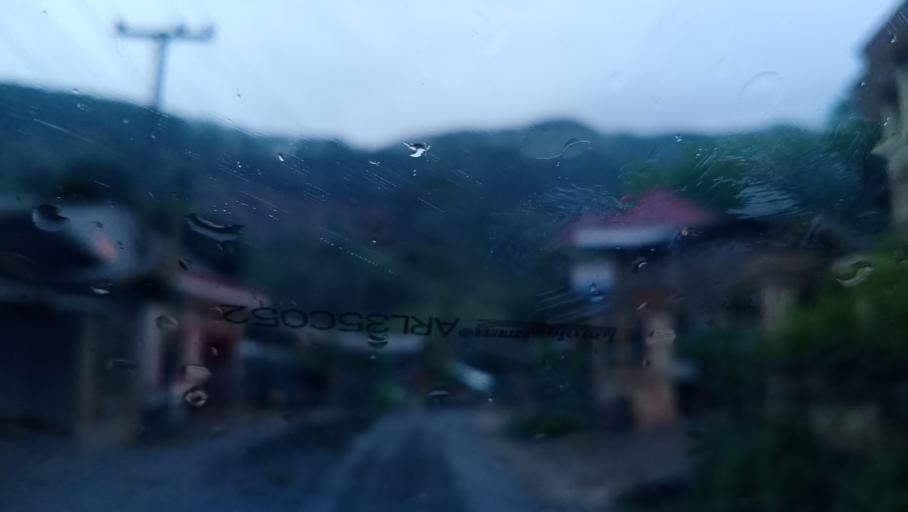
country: LA
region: Phongsali
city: Khoa
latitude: 21.0753
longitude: 102.5022
